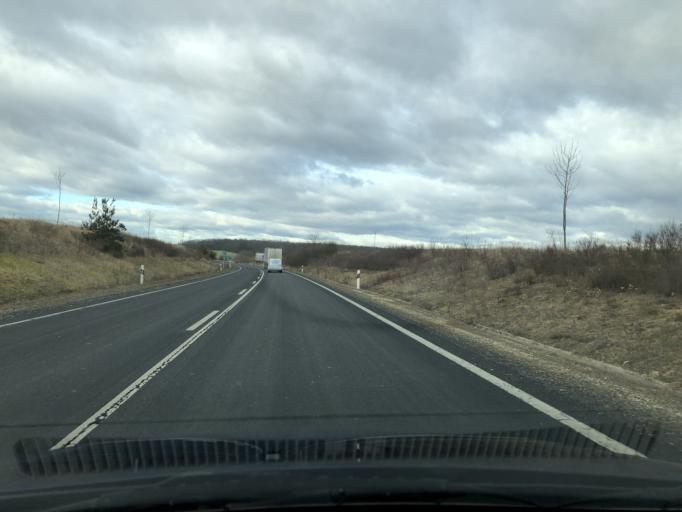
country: AT
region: Burgenland
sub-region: Politischer Bezirk Oberwart
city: Schachendorf
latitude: 47.2474
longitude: 16.5056
